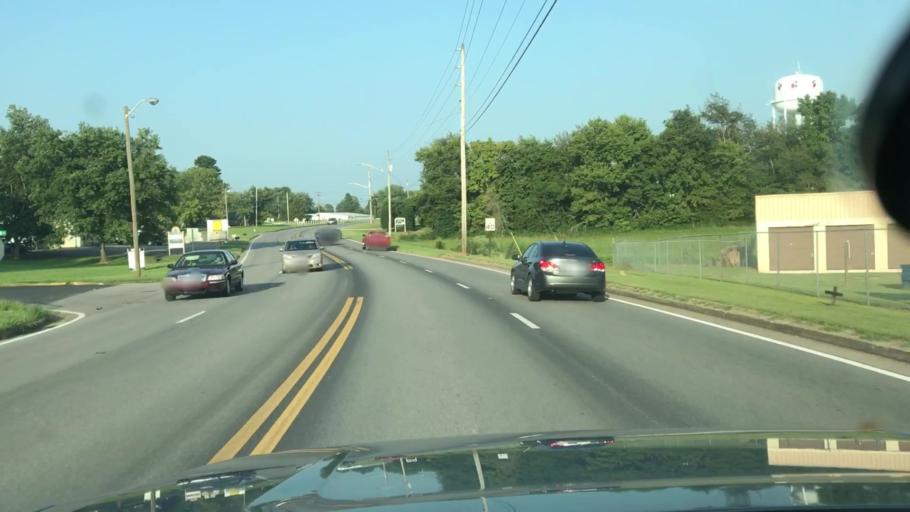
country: US
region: Tennessee
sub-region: Sumner County
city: Portland
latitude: 36.5773
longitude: -86.5022
